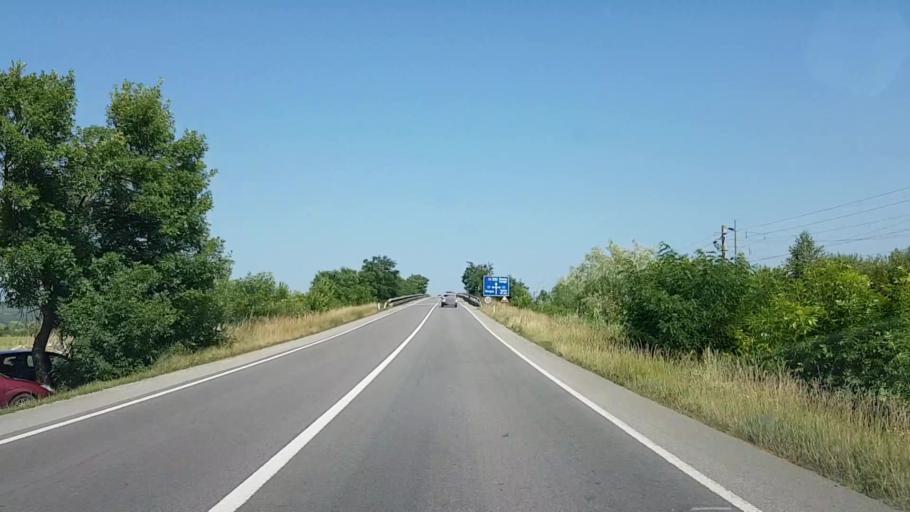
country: RO
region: Bistrita-Nasaud
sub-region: Comuna Sintereag
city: Cociu
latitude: 47.1830
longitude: 24.2285
